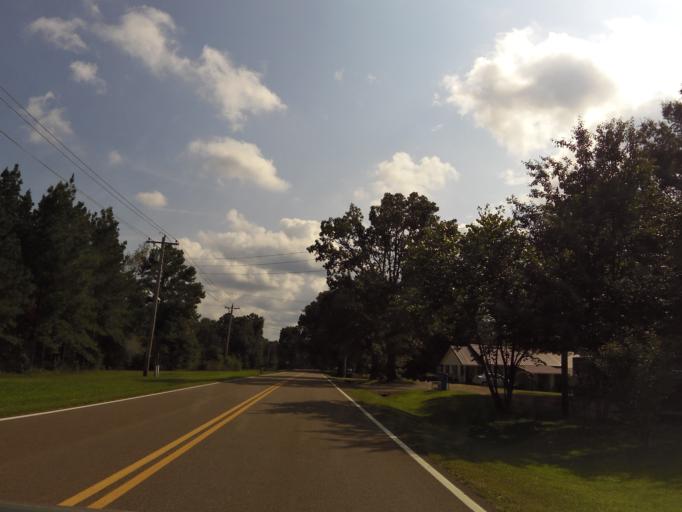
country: US
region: Tennessee
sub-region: McNairy County
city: Adamsville
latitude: 35.0933
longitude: -88.3811
